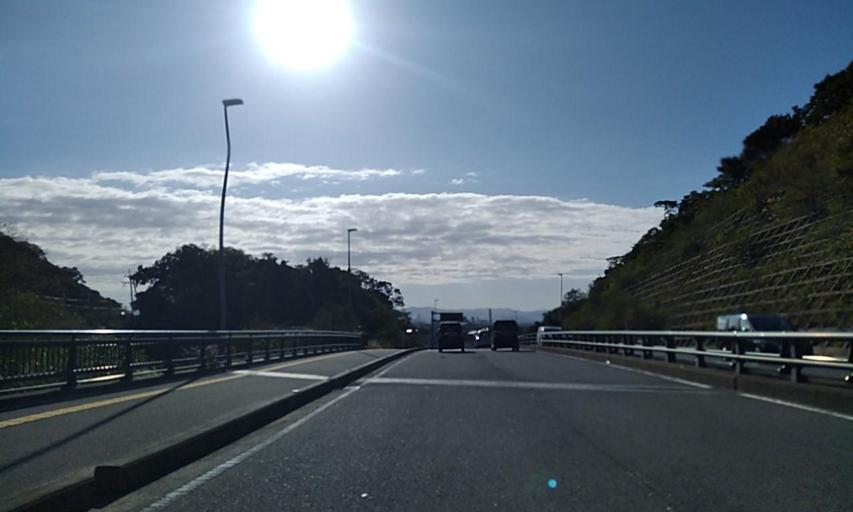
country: JP
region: Wakayama
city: Minato
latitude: 34.2637
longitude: 135.0989
